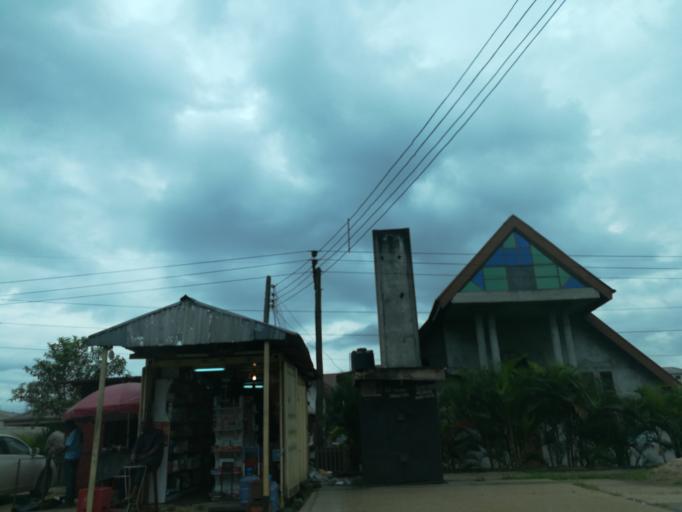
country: NG
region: Rivers
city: Port Harcourt
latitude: 4.8390
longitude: 7.0355
